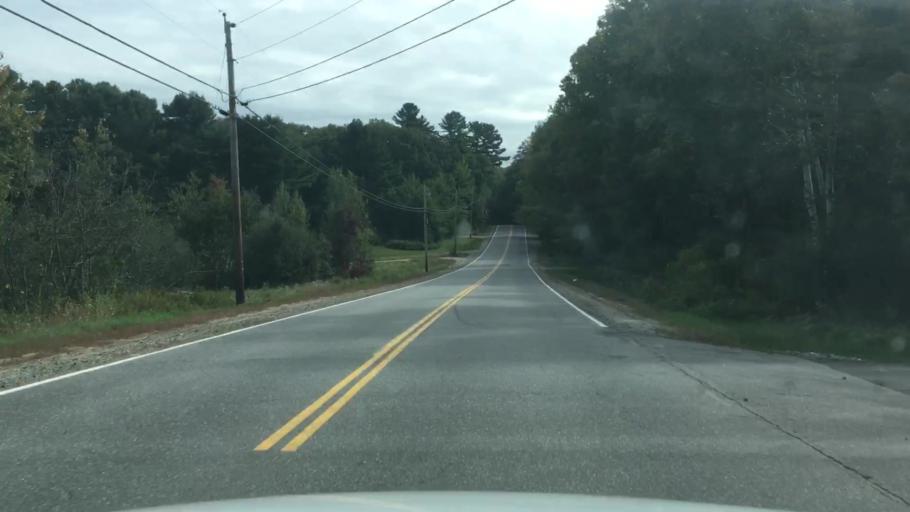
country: US
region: Maine
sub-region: Sagadahoc County
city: Topsham
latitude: 43.9425
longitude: -70.0267
